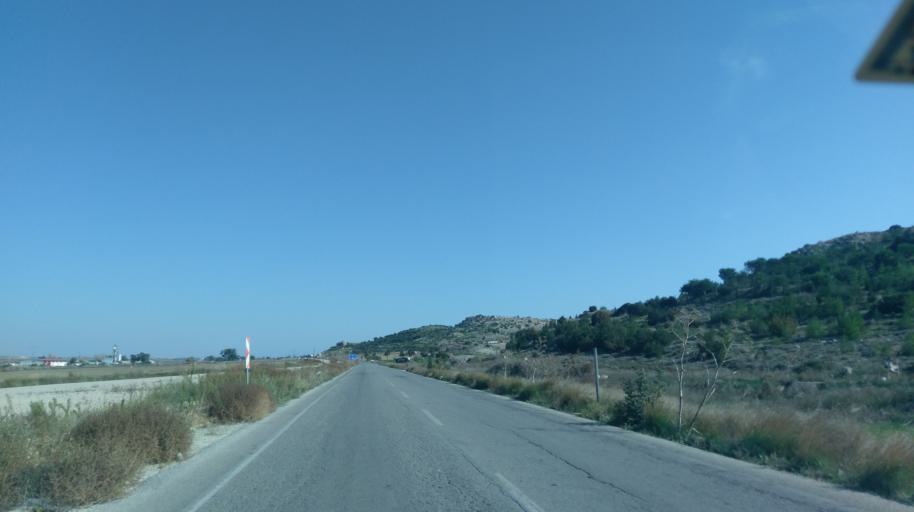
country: CY
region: Ammochostos
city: Trikomo
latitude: 35.3485
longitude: 33.9895
